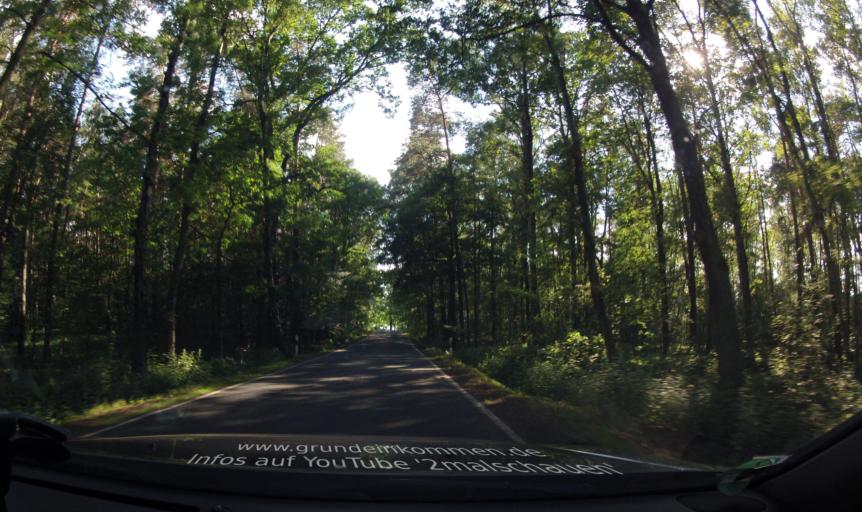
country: DE
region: Saxony
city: Falkenhain
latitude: 51.4178
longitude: 12.9000
